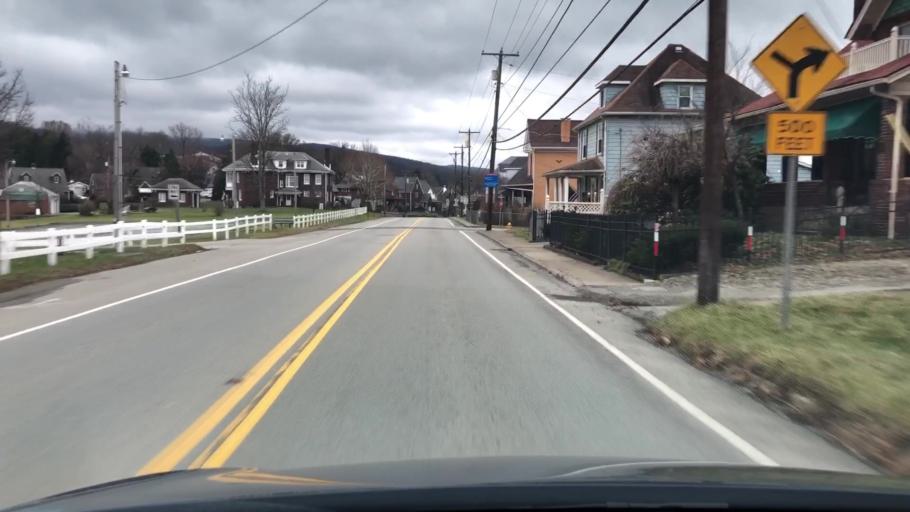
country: US
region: Pennsylvania
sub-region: Fayette County
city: Connellsville
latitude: 40.0264
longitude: -79.5808
